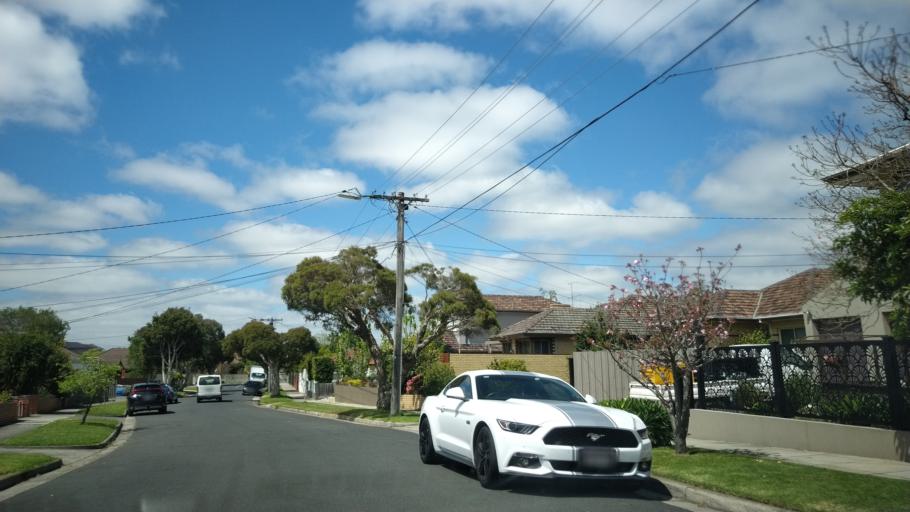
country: AU
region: Victoria
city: Murrumbeena
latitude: -37.9033
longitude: 145.0678
